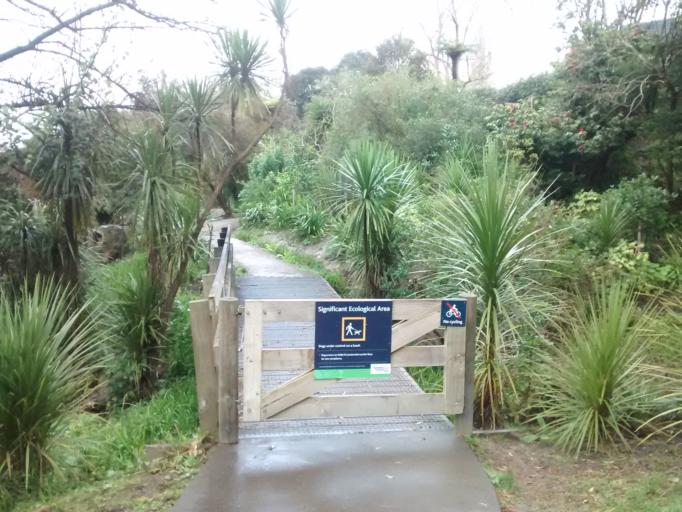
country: NZ
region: Auckland
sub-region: Auckland
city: Rosebank
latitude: -36.8560
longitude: 174.7160
